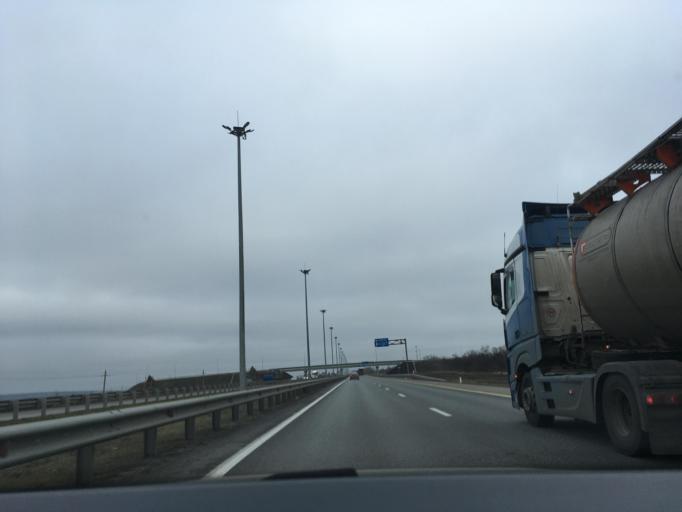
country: RU
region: Rostov
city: Glubokiy
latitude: 48.4981
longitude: 40.3410
